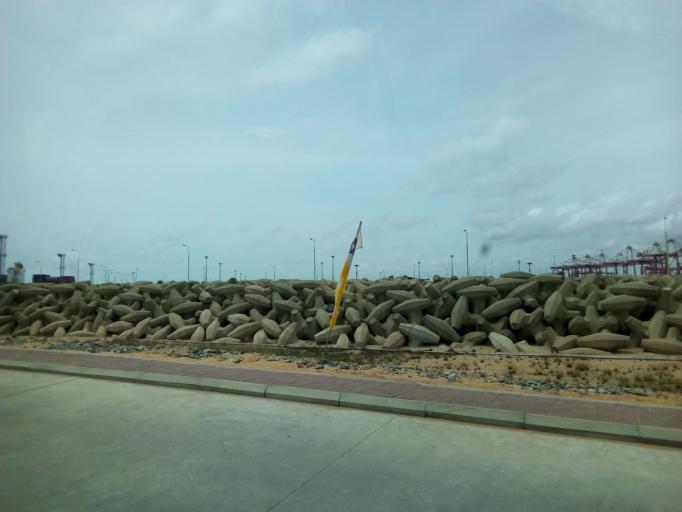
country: LK
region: Western
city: Colombo
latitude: 6.9397
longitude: 79.8391
